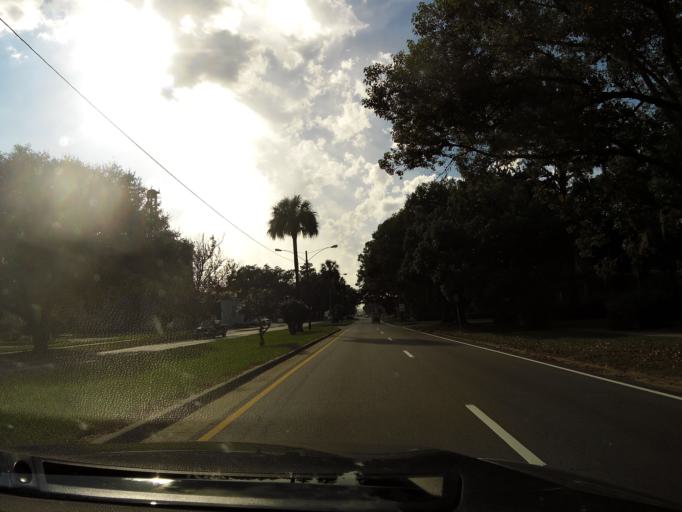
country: US
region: Georgia
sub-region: Brooks County
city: Quitman
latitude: 30.7852
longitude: -83.5647
